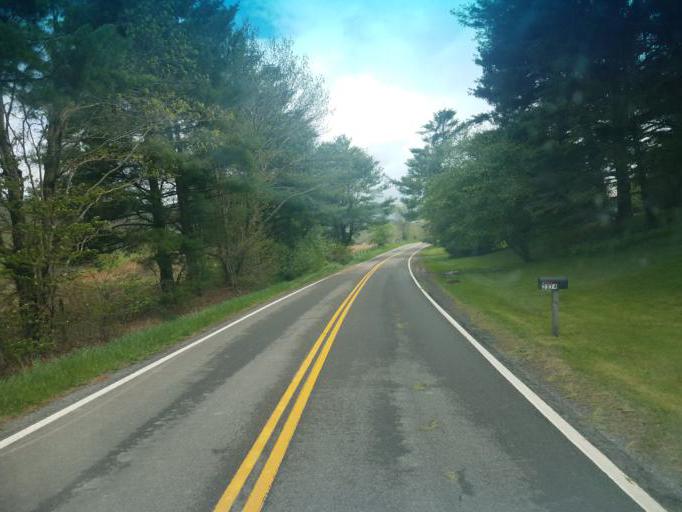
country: US
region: Virginia
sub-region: Smyth County
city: Atkins
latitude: 36.9989
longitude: -81.3770
